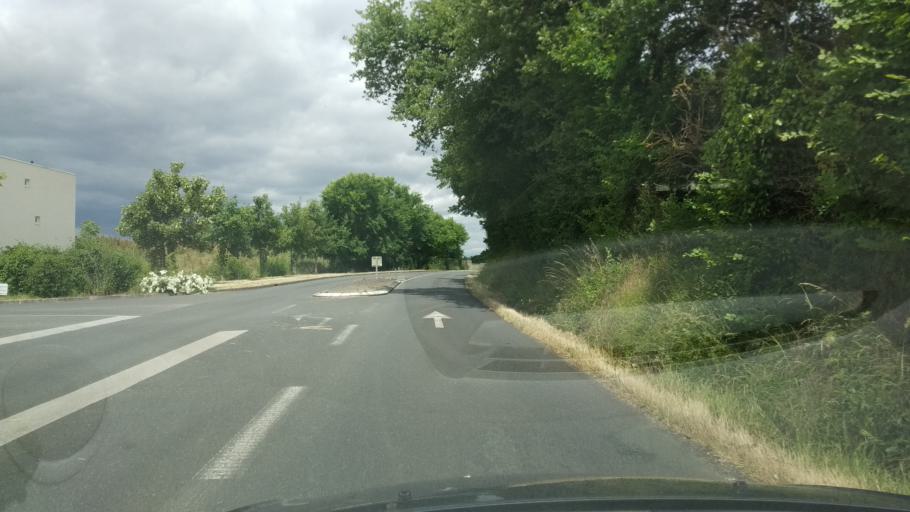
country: FR
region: Poitou-Charentes
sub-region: Departement de la Vienne
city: Vouneuil-sous-Biard
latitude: 46.5665
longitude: 0.2703
